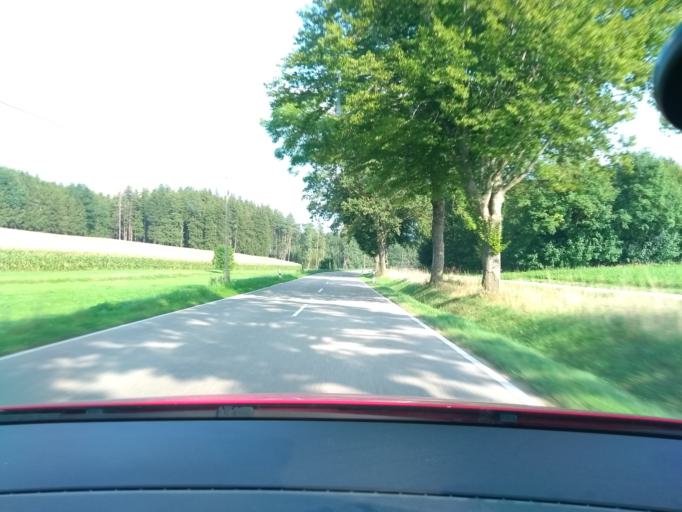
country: DE
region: Bavaria
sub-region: Upper Bavaria
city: Schwabhausen
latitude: 48.3883
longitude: 11.3286
